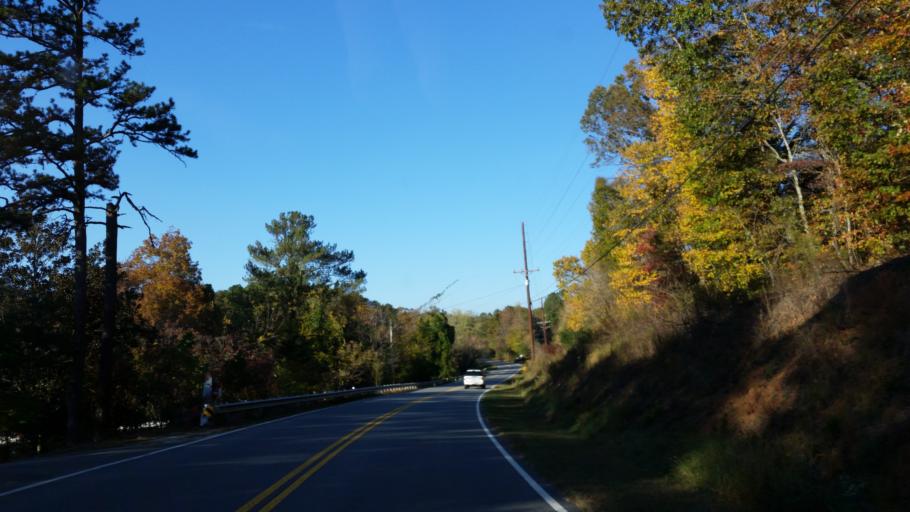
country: US
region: Georgia
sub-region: Gilmer County
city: Ellijay
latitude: 34.6589
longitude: -84.4733
